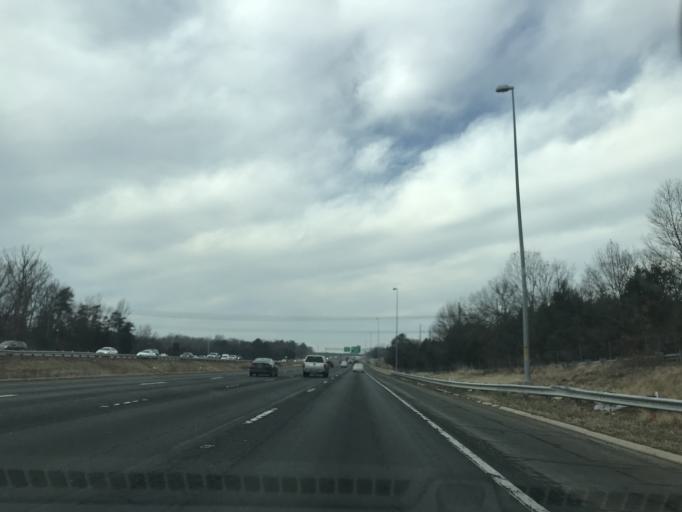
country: US
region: Virginia
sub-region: Prince William County
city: Linton Hall
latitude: 38.7990
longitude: -77.5611
